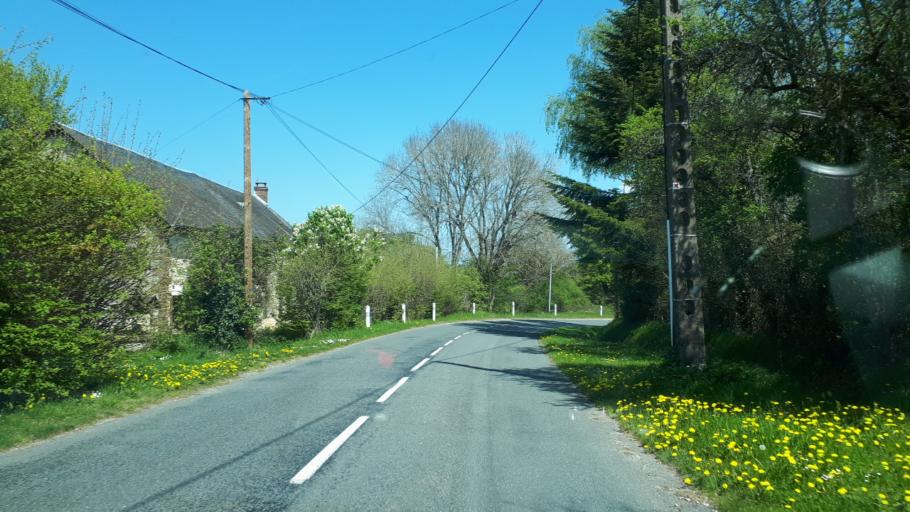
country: FR
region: Centre
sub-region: Departement du Cher
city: Henrichemont
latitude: 47.3044
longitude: 2.6211
